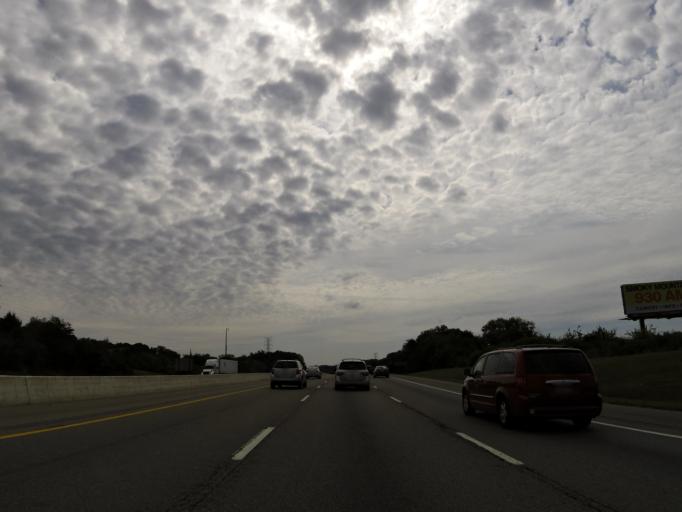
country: US
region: Tennessee
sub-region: Knox County
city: Mascot
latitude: 36.0089
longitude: -83.8191
